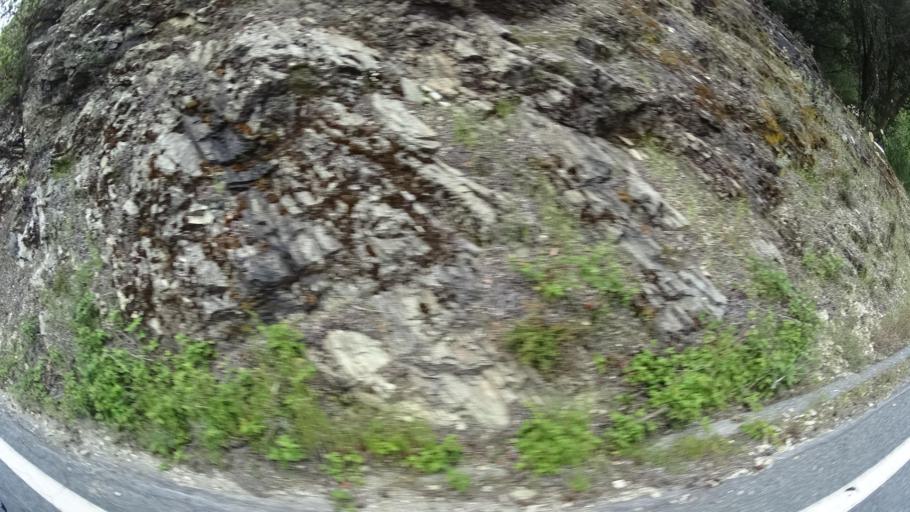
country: US
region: California
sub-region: Humboldt County
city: Willow Creek
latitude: 41.2774
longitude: -123.5947
